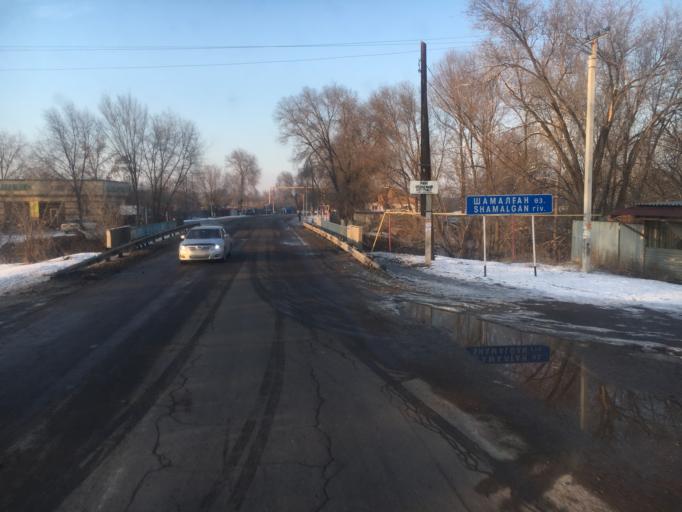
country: KZ
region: Almaty Oblysy
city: Burunday
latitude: 43.3661
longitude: 76.6416
